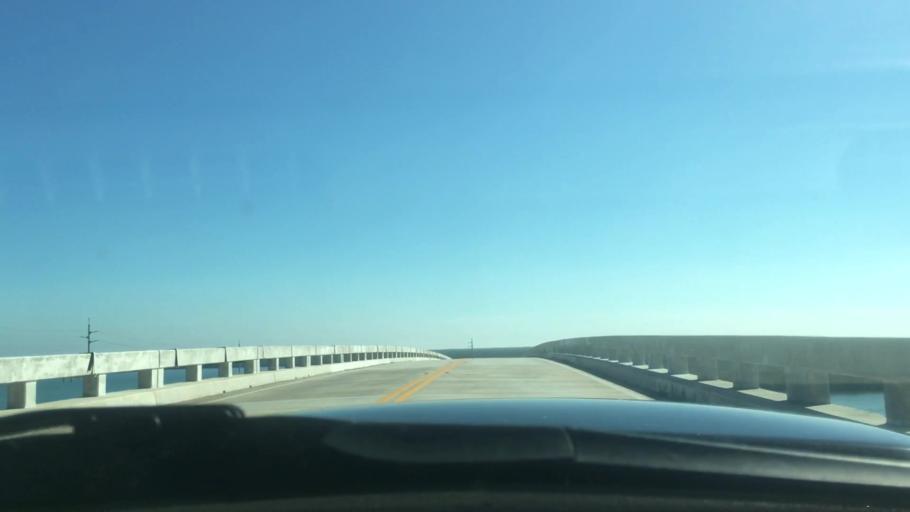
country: US
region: Florida
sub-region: Monroe County
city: North Key Largo
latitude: 25.2874
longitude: -80.3687
